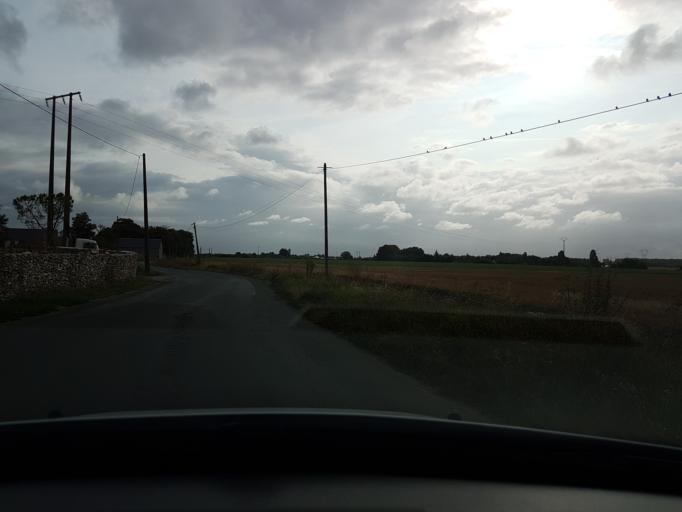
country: FR
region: Centre
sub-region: Departement d'Indre-et-Loire
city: Veretz
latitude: 47.3356
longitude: 0.8216
